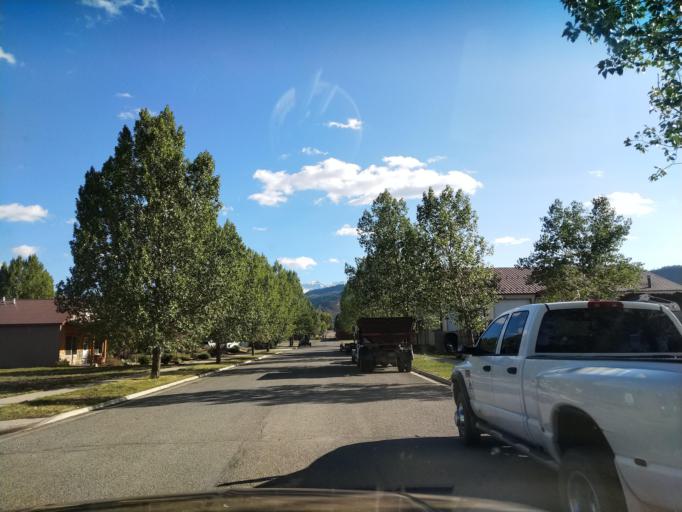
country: US
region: Colorado
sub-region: Ouray County
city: Ouray
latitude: 38.1572
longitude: -107.7576
